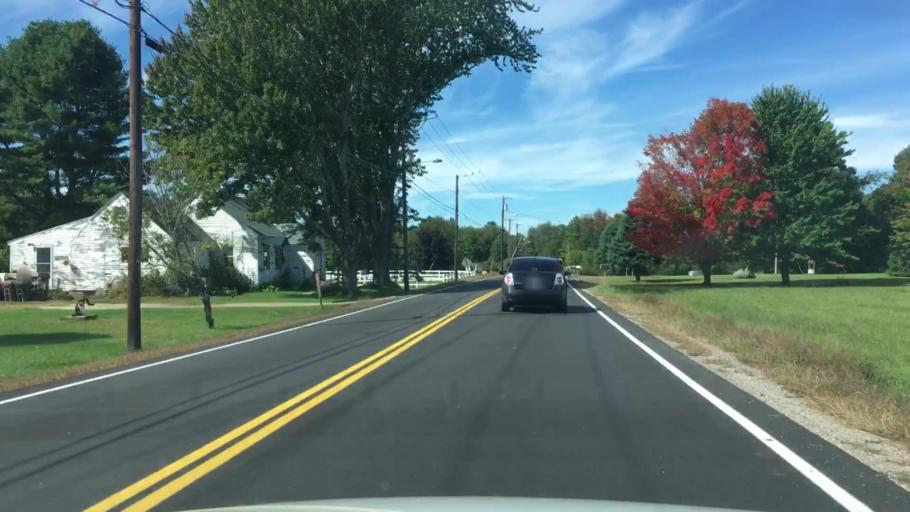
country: US
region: Maine
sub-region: York County
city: Biddeford
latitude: 43.5419
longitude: -70.4939
